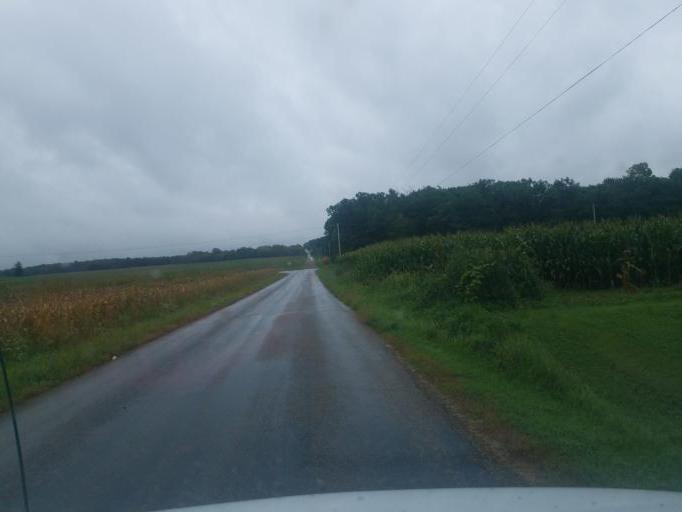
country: US
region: Ohio
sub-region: Wayne County
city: West Salem
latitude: 40.9300
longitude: -82.1108
